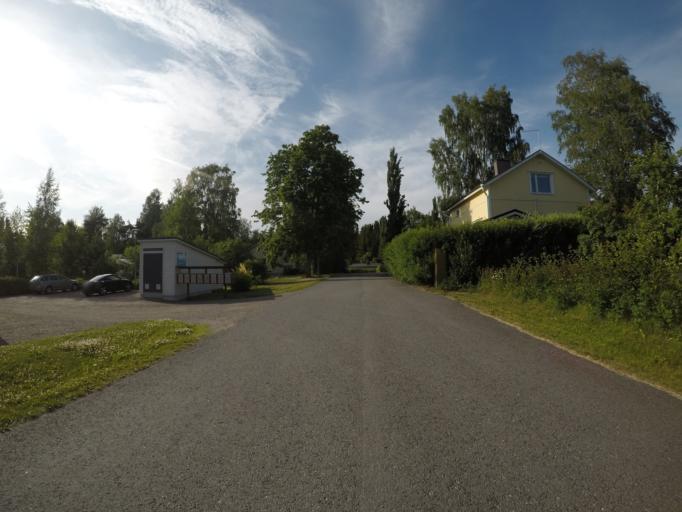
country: FI
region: Haeme
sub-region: Haemeenlinna
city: Haemeenlinna
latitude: 60.9800
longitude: 24.4159
